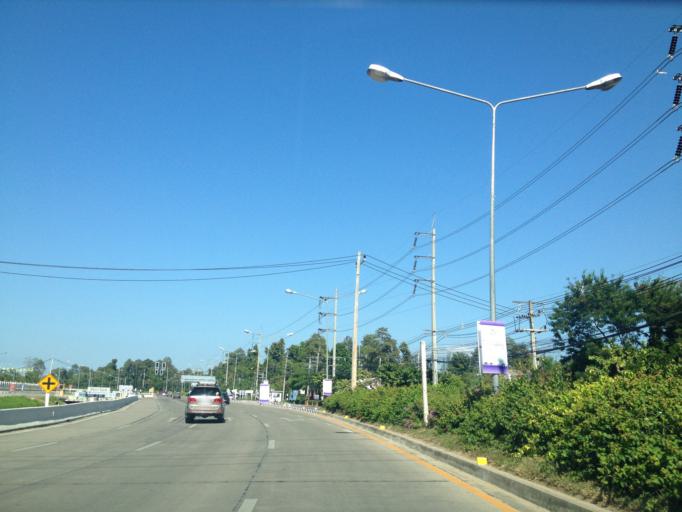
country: TH
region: Chiang Mai
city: Chiang Mai
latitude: 18.8216
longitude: 98.9650
